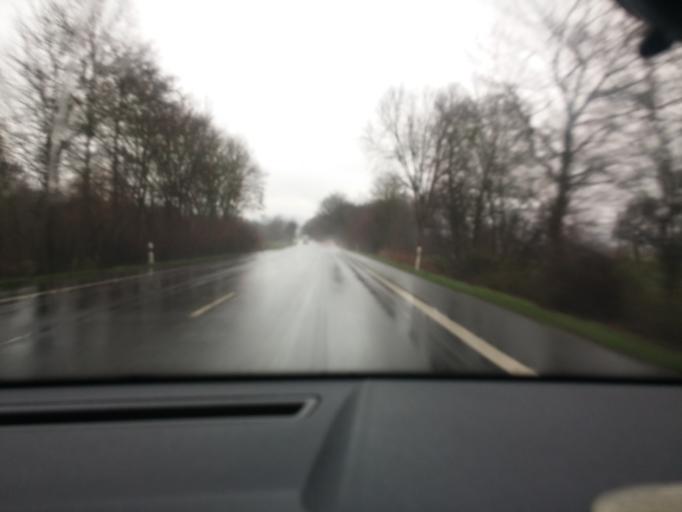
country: DE
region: Hesse
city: Gross-Bieberau
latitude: 49.7895
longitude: 8.8511
